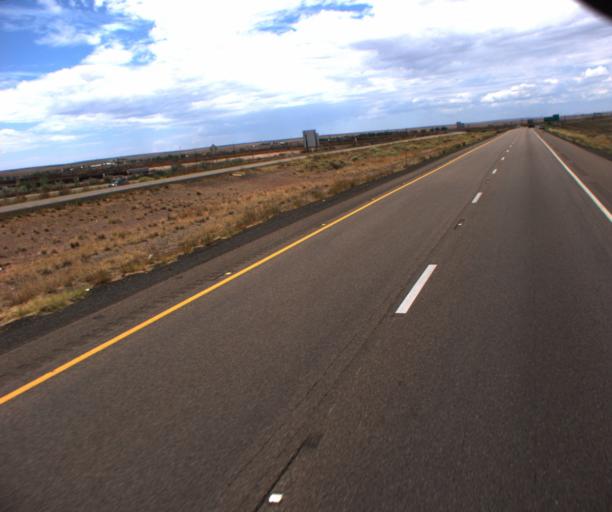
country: US
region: Arizona
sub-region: Navajo County
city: Holbrook
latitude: 34.9074
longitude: -110.1824
